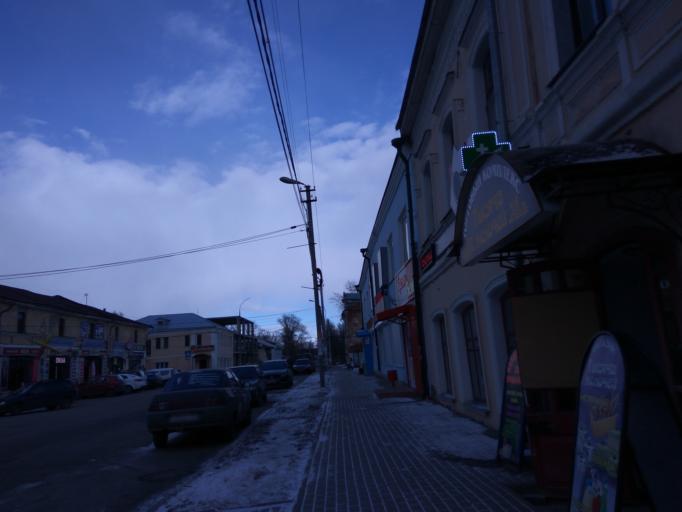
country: RU
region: Jaroslavl
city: Rostov
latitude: 57.1869
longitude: 39.4160
